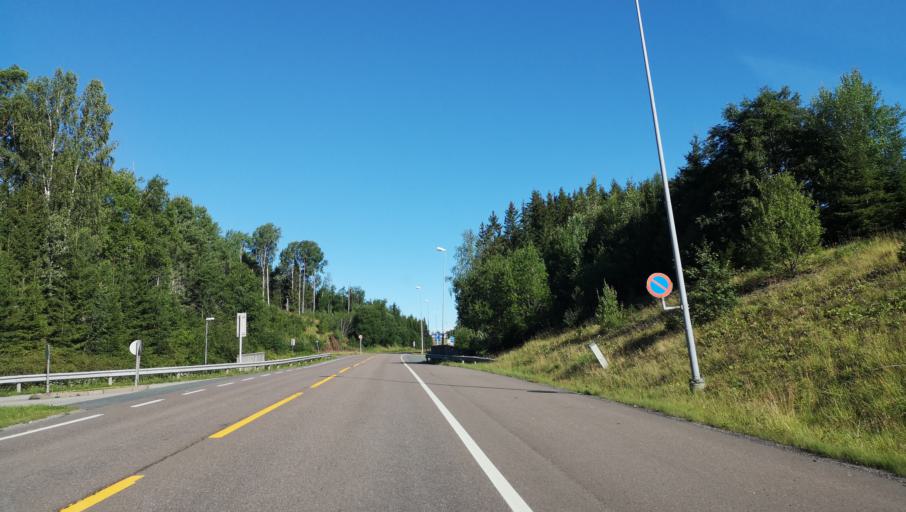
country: NO
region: Ostfold
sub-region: Spydeberg
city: Spydeberg
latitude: 59.6049
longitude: 11.1009
